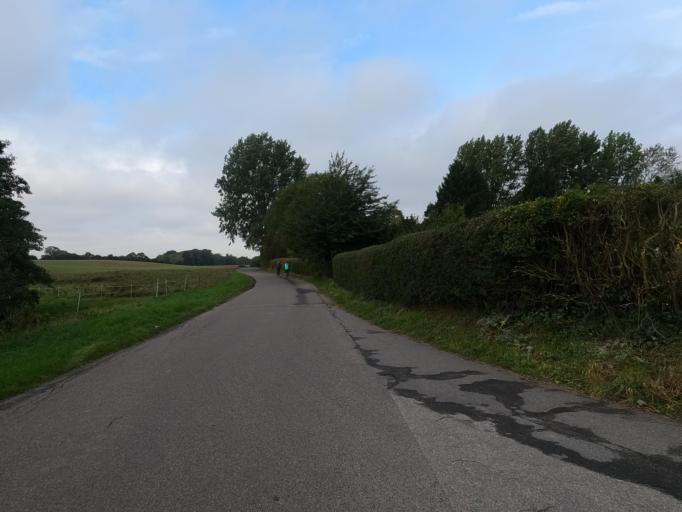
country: DE
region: Schleswig-Holstein
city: Neukirchen
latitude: 54.3092
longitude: 11.0510
